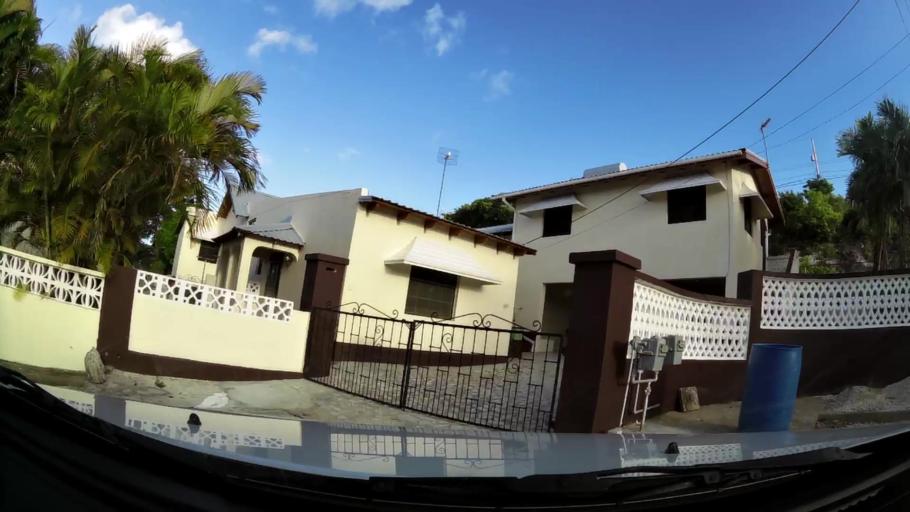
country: BB
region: Christ Church
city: Oistins
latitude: 13.0689
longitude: -59.5518
